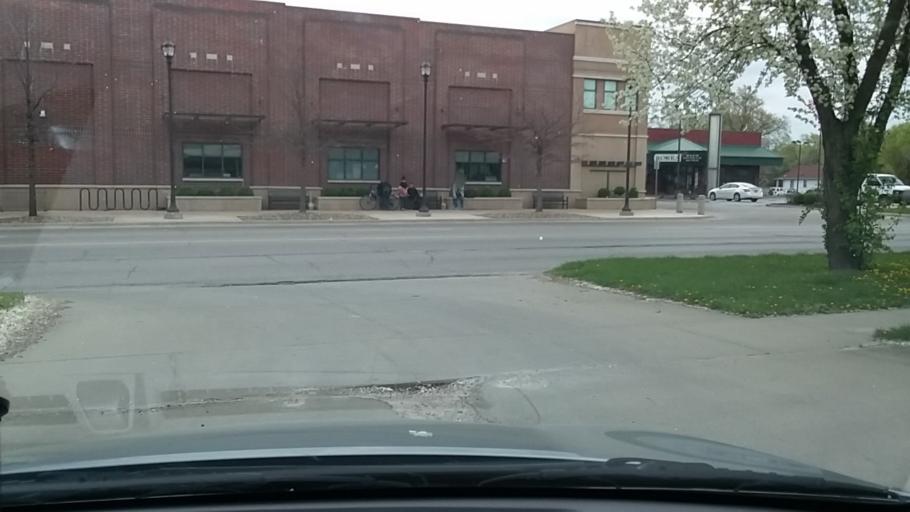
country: US
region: Kansas
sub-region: Douglas County
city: Lawrence
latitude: 38.9519
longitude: -95.2361
